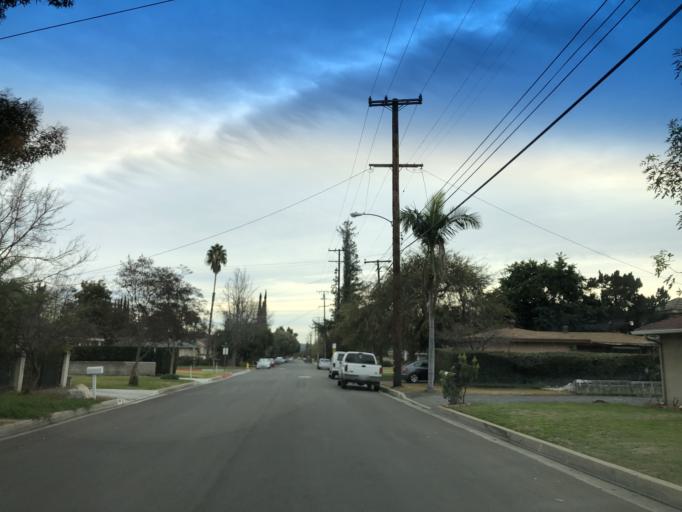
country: US
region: California
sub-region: Los Angeles County
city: Arcadia
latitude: 34.1353
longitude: -118.0205
